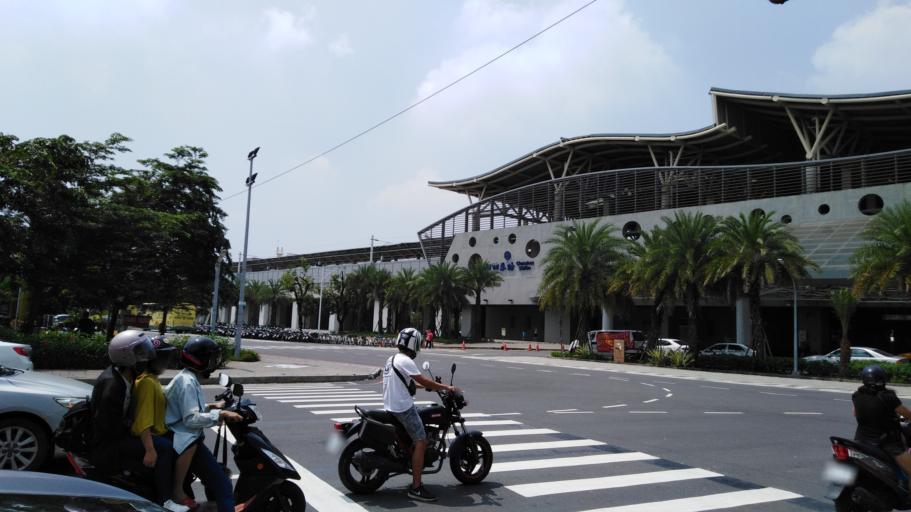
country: TW
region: Taiwan
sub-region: Pingtung
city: Pingtung
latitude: 22.5501
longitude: 120.5368
